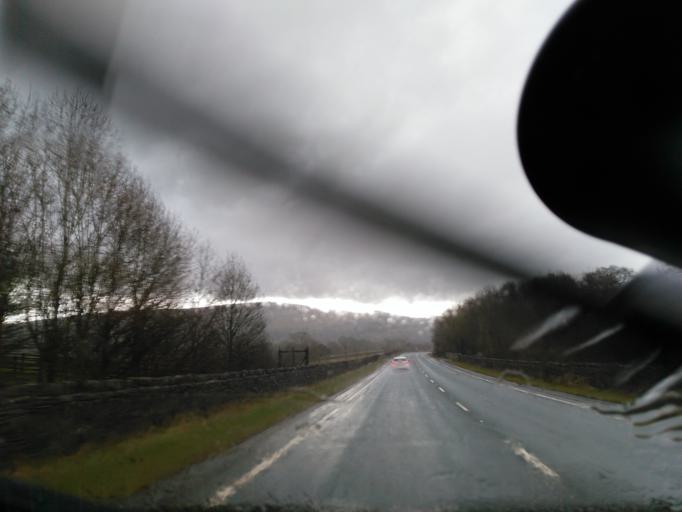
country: GB
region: England
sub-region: Bradford
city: Addingham
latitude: 53.9762
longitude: -1.9040
